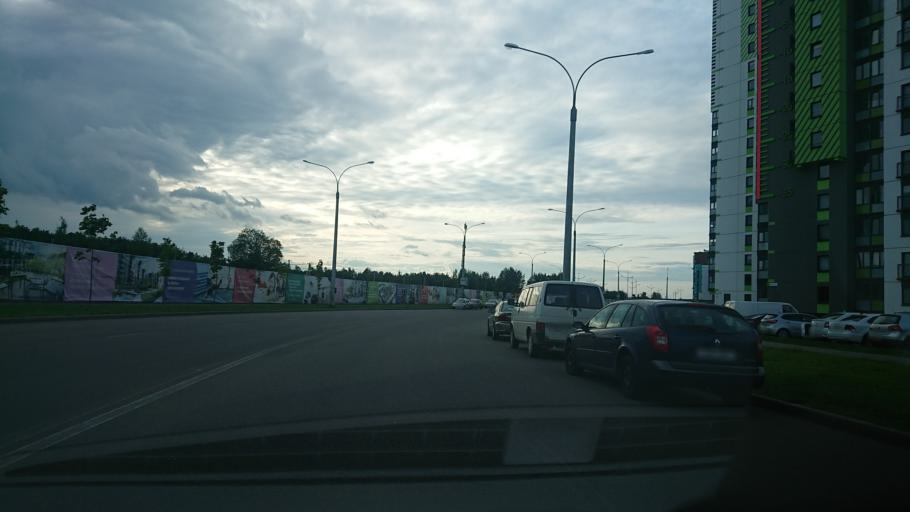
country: BY
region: Minsk
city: Borovlyany
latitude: 53.9527
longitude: 27.6643
